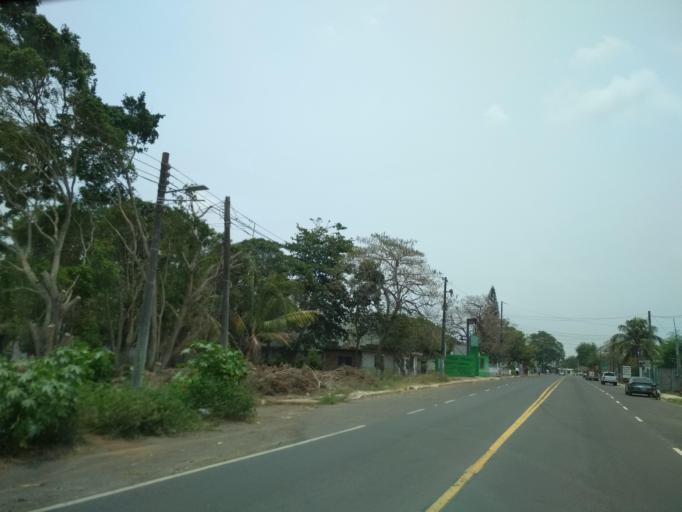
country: MX
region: Veracruz
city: Manlio Fabio Altamirano
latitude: 19.1351
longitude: -96.2983
